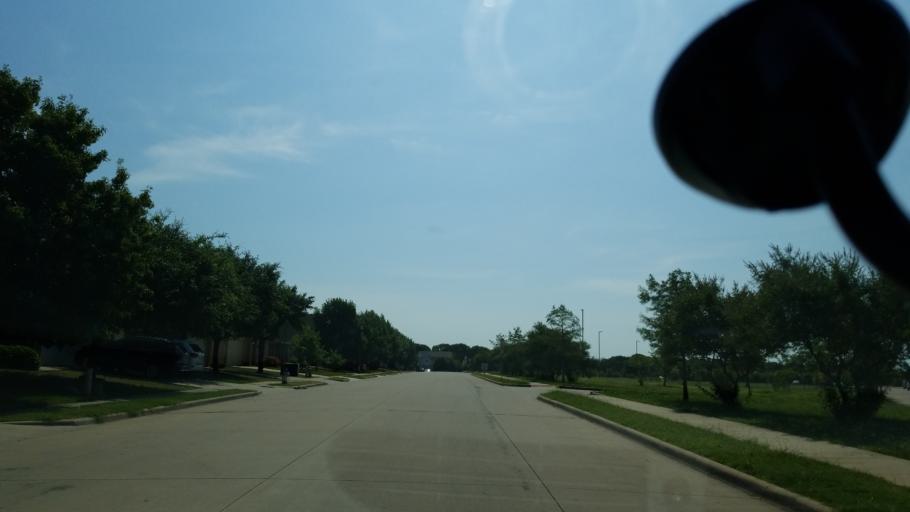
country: US
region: Texas
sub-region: Dallas County
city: Cockrell Hill
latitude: 32.7120
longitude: -96.8688
